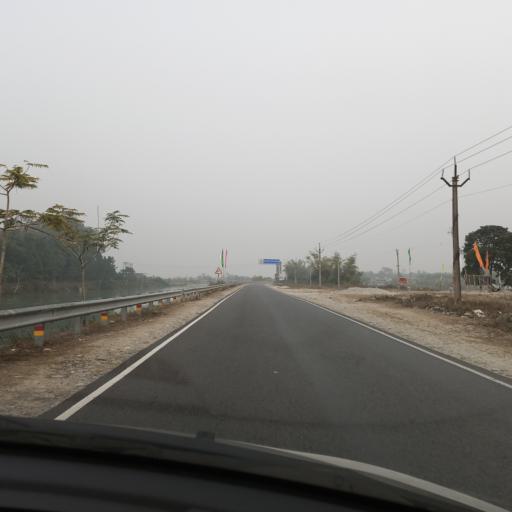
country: IN
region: West Bengal
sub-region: Jalpaiguri
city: Odlabari
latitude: 26.7330
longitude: 88.5758
